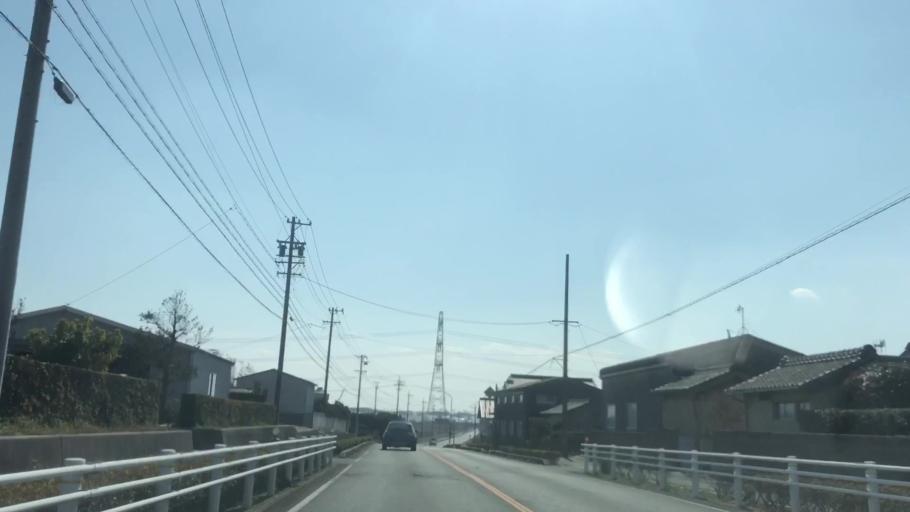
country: JP
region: Aichi
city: Tahara
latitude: 34.6434
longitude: 137.2392
